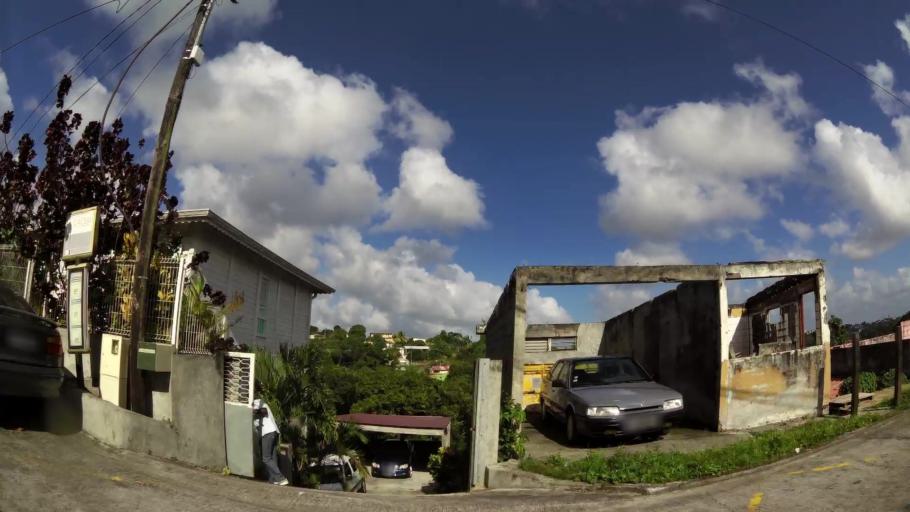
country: MQ
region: Martinique
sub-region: Martinique
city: Fort-de-France
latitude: 14.6422
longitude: -61.0763
